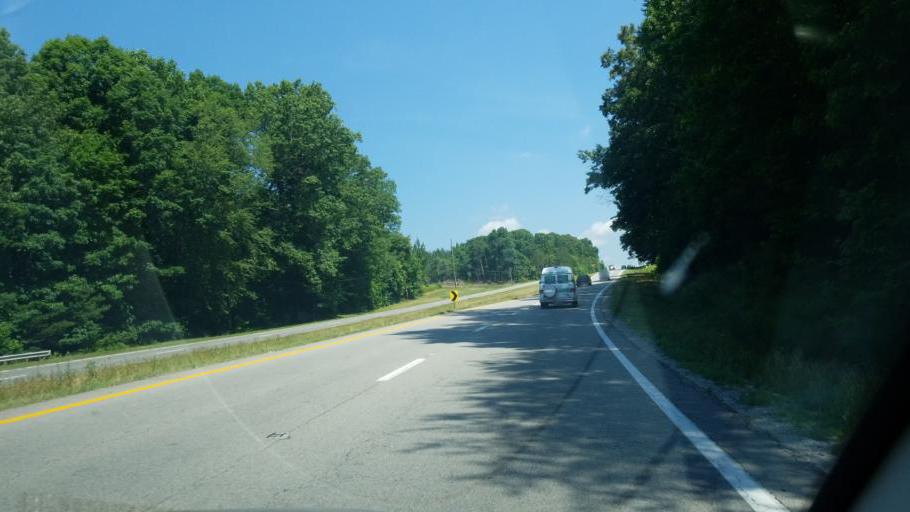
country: US
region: Virginia
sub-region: Pittsylvania County
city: Chatham
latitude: 36.7806
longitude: -79.3937
